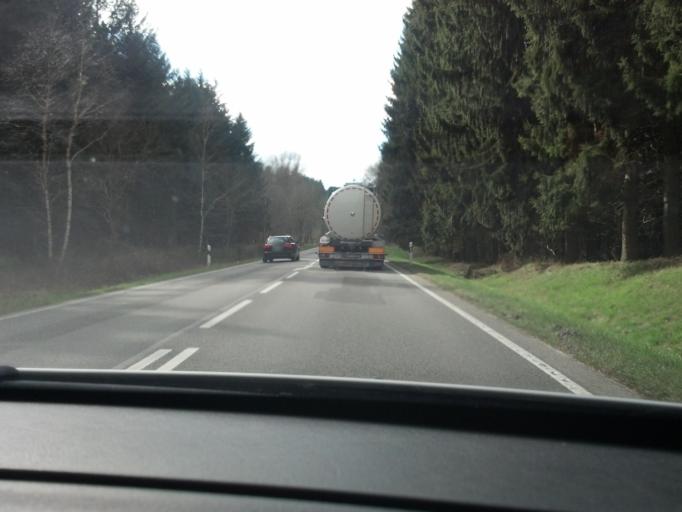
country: DE
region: Mecklenburg-Vorpommern
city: Malchow
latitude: 53.3652
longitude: 12.4053
